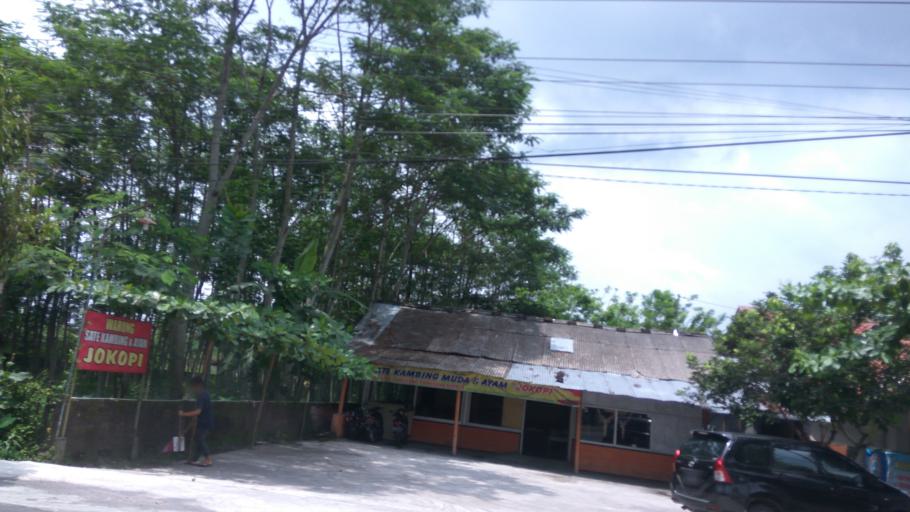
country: ID
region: Daerah Istimewa Yogyakarta
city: Melati
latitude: -7.7299
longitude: 110.3794
